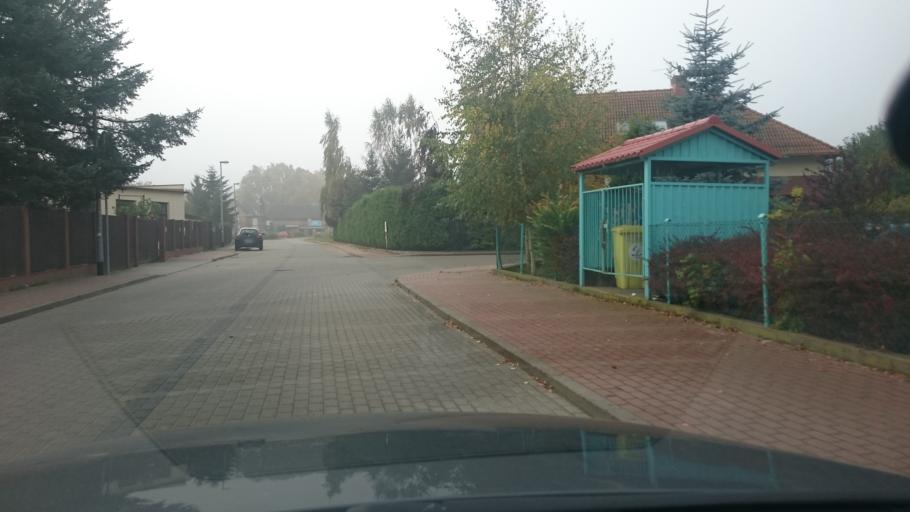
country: PL
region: Pomeranian Voivodeship
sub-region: Gdynia
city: Wielki Kack
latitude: 54.4621
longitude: 18.4933
